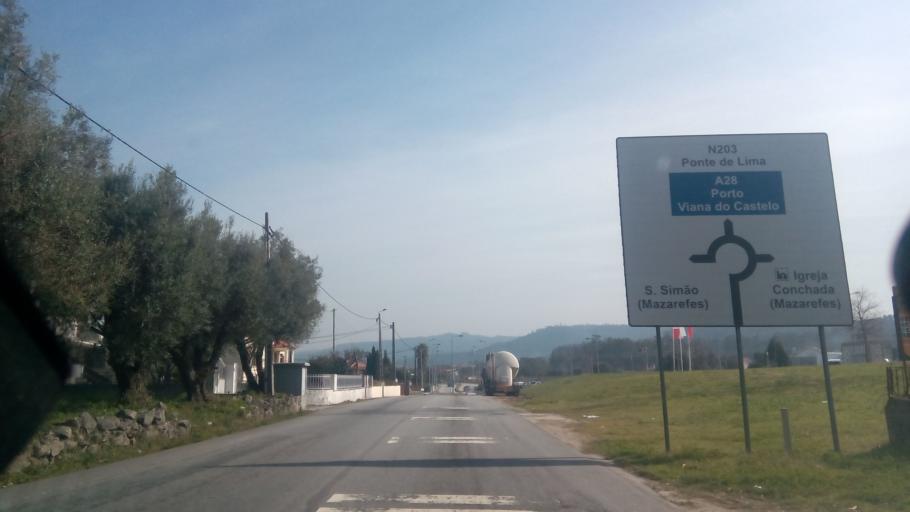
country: PT
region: Viana do Castelo
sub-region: Viana do Castelo
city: Darque
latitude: 41.6810
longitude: -8.7684
